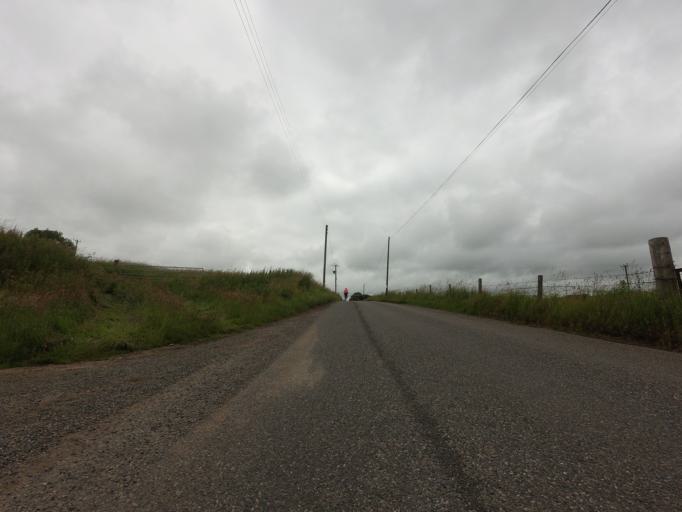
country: GB
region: Scotland
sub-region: Aberdeenshire
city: Turriff
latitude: 57.5397
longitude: -2.3697
